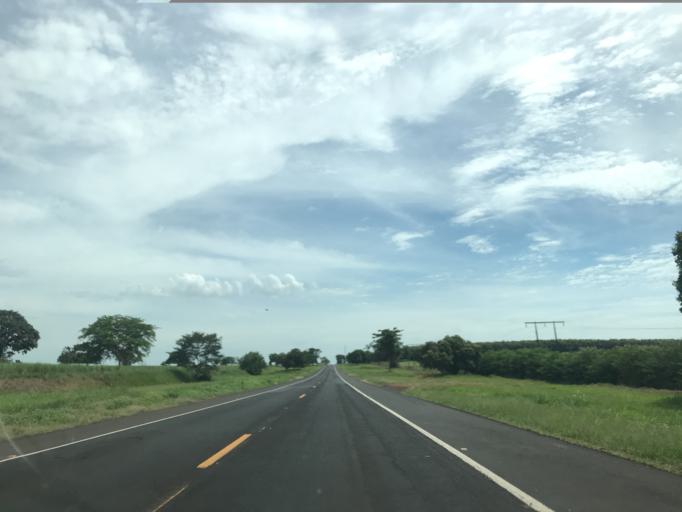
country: BR
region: Sao Paulo
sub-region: Nova Granada
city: Nova Granada
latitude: -20.4009
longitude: -49.2436
